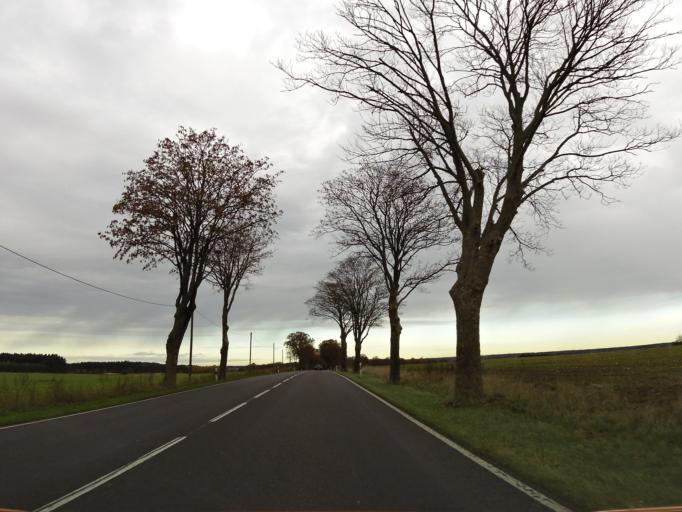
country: DE
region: Saxony-Anhalt
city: Letzlingen
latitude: 52.4306
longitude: 11.4826
